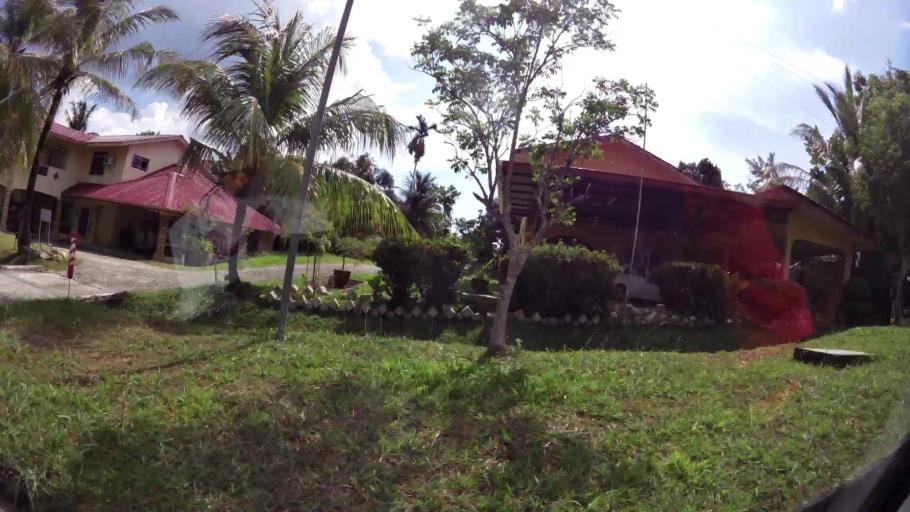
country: BN
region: Brunei and Muara
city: Bandar Seri Begawan
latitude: 4.9586
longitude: 114.9590
